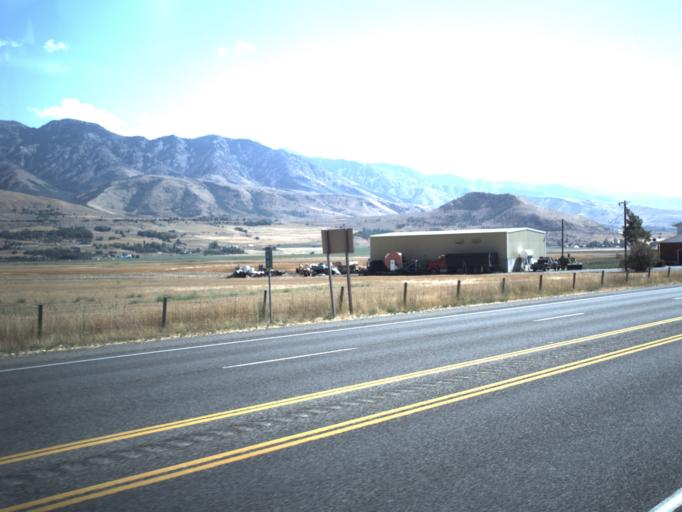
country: US
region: Utah
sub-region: Cache County
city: Lewiston
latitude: 41.9951
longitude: -111.8129
